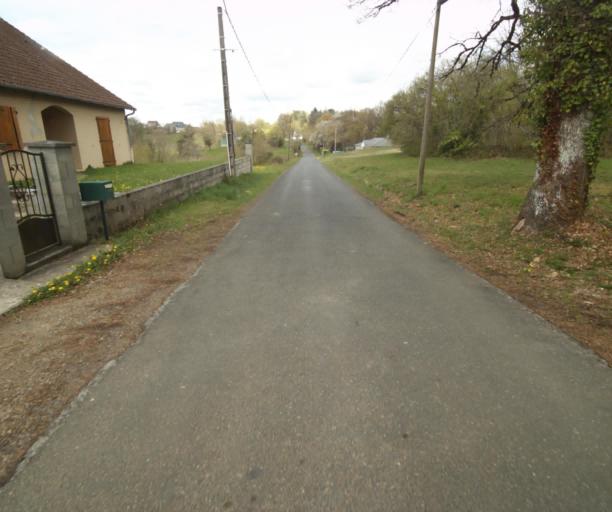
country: FR
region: Limousin
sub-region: Departement de la Correze
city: Sainte-Fortunade
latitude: 45.1980
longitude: 1.8562
